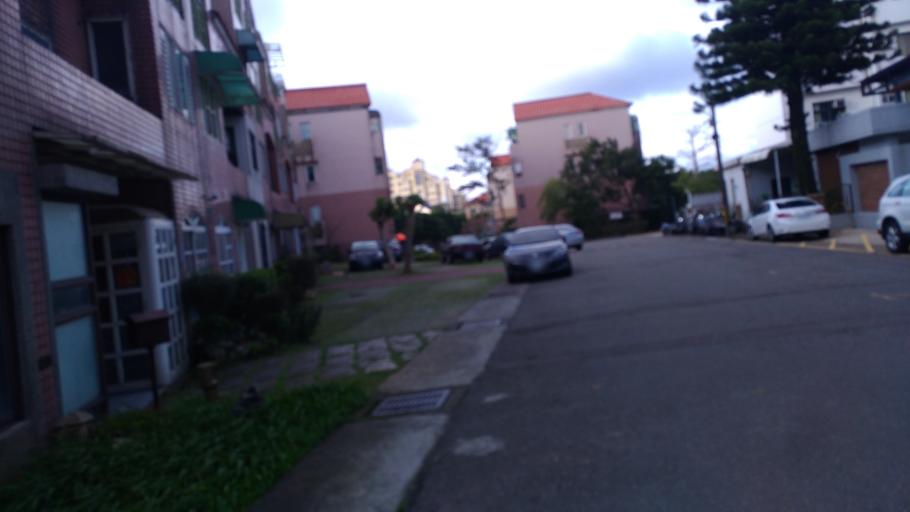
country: TW
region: Taiwan
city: Daxi
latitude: 24.8832
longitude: 121.1732
